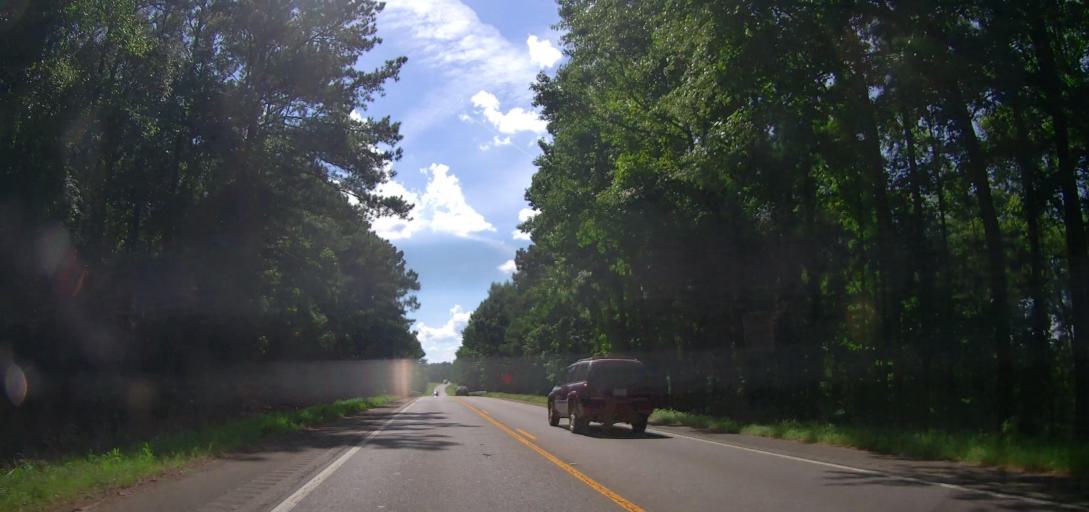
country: US
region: Alabama
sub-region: Pickens County
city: Gordo
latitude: 33.2846
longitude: -87.8448
